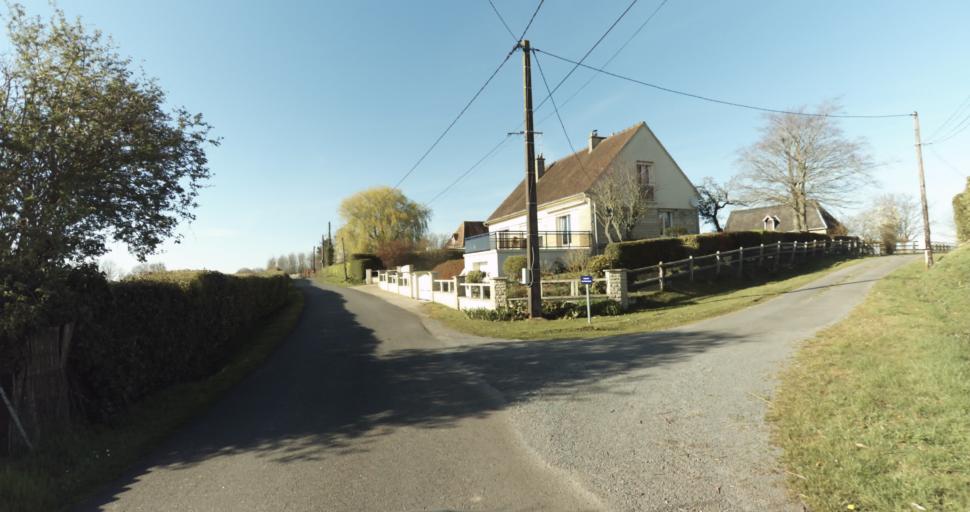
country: FR
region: Lower Normandy
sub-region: Departement du Calvados
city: Saint-Pierre-sur-Dives
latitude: 49.0476
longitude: 0.0306
